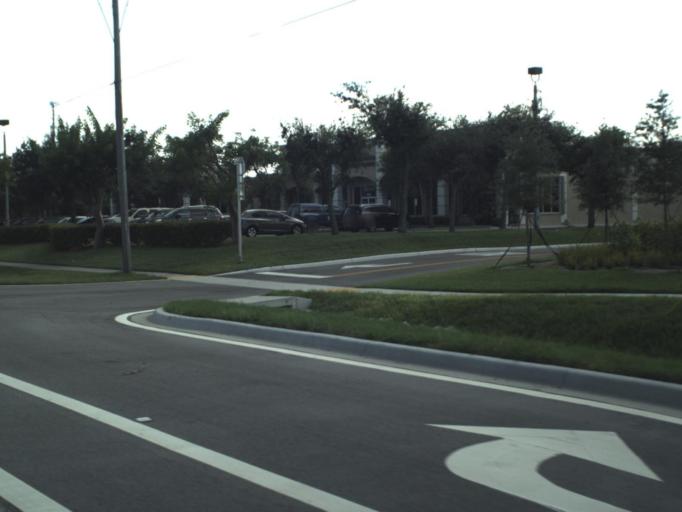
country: US
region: Florida
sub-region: Palm Beach County
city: Royal Palm Beach
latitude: 26.7043
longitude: -80.2012
